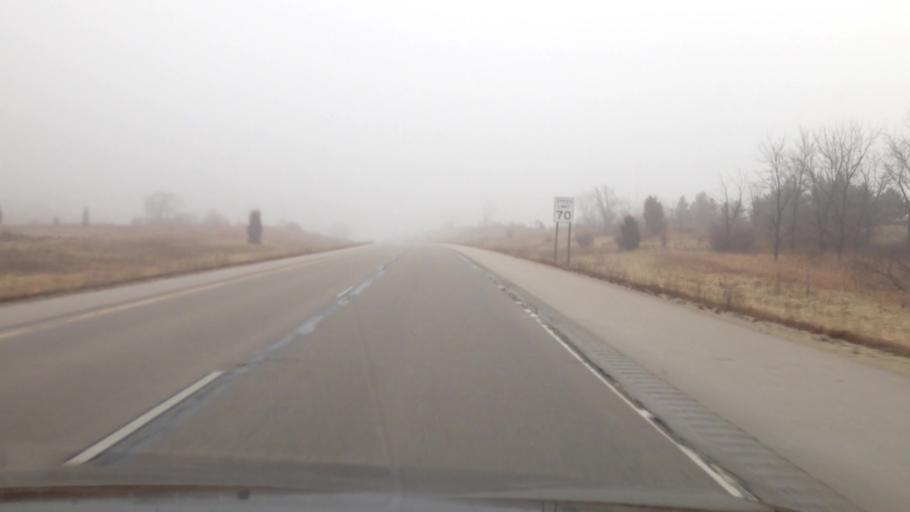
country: US
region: Wisconsin
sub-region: Walworth County
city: East Troy
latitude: 42.7547
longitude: -88.4362
